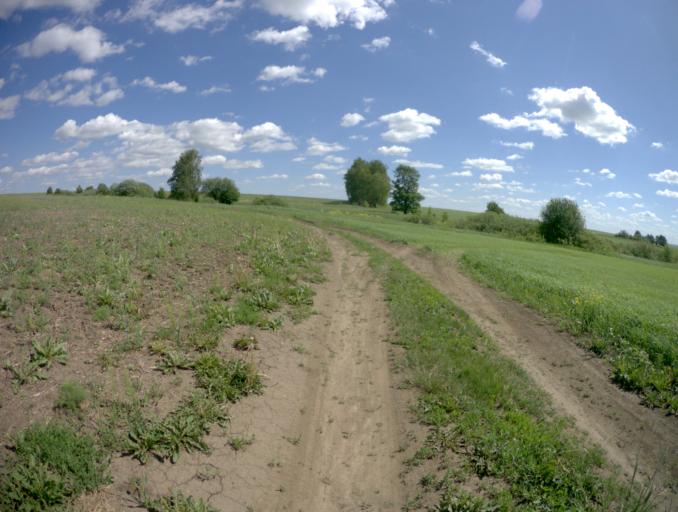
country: RU
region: Ivanovo
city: Gavrilov Posad
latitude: 56.4527
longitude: 40.2183
